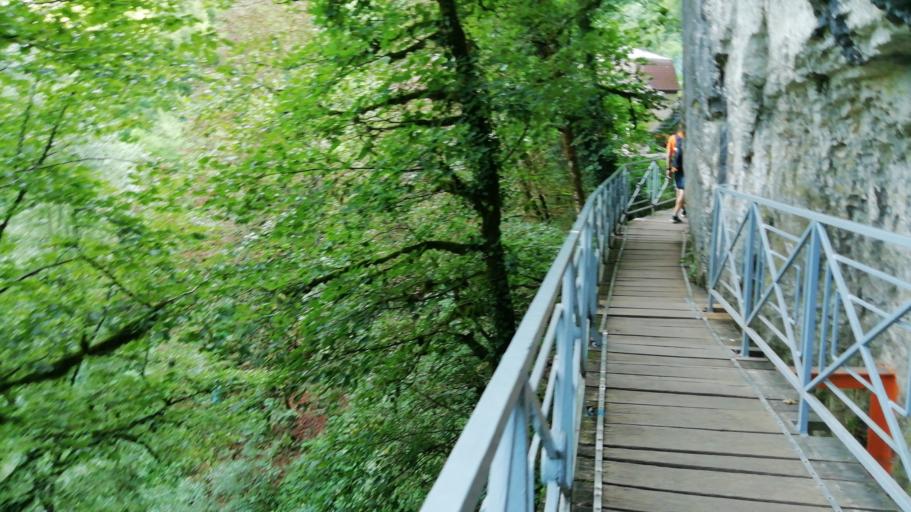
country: FR
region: Rhone-Alpes
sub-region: Departement de la Haute-Savoie
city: Chavanod
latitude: 45.8959
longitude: 6.0380
